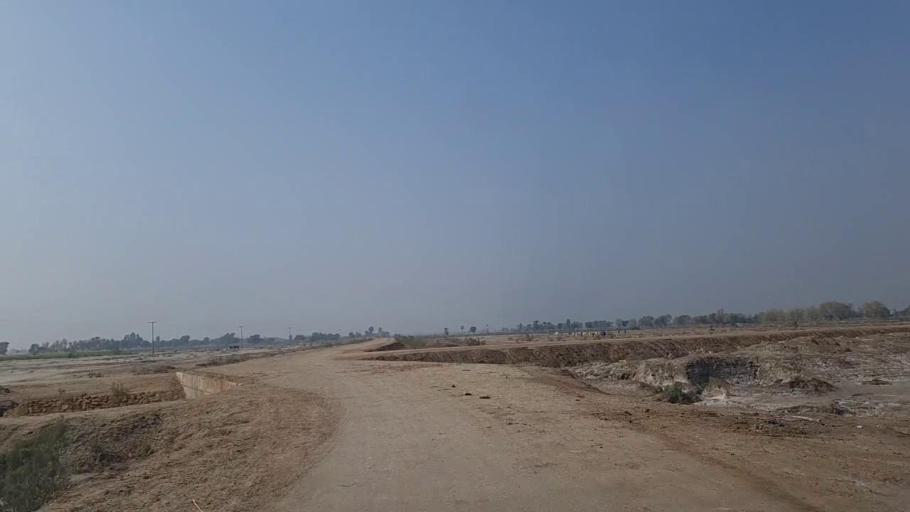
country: PK
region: Sindh
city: Nawabshah
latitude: 26.3599
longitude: 68.4304
